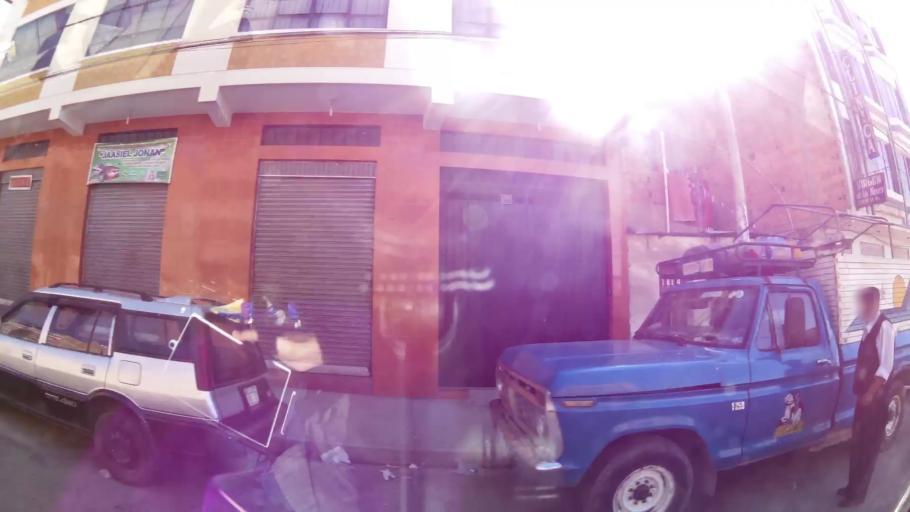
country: BO
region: La Paz
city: La Paz
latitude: -16.5136
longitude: -68.1441
